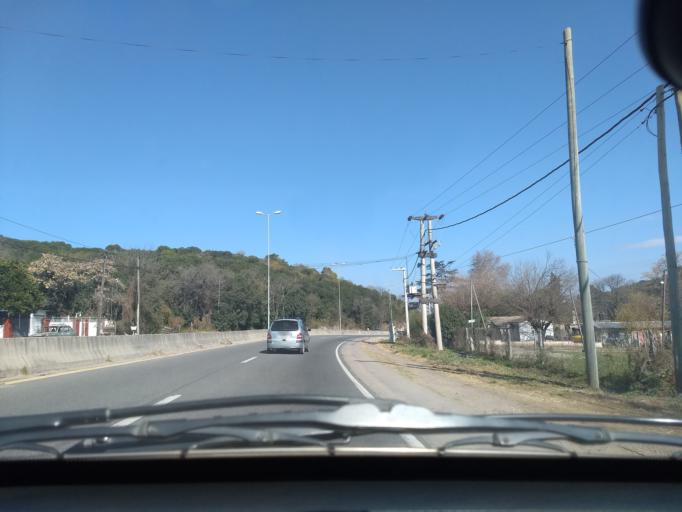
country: AR
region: Cordoba
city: Rio Ceballos
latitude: -31.1673
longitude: -64.3021
